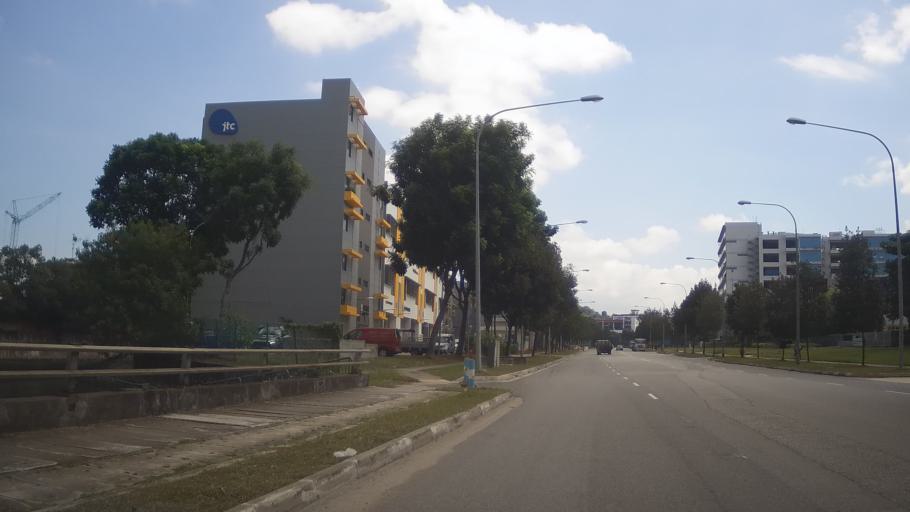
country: SG
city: Singapore
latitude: 1.3118
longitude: 103.6988
